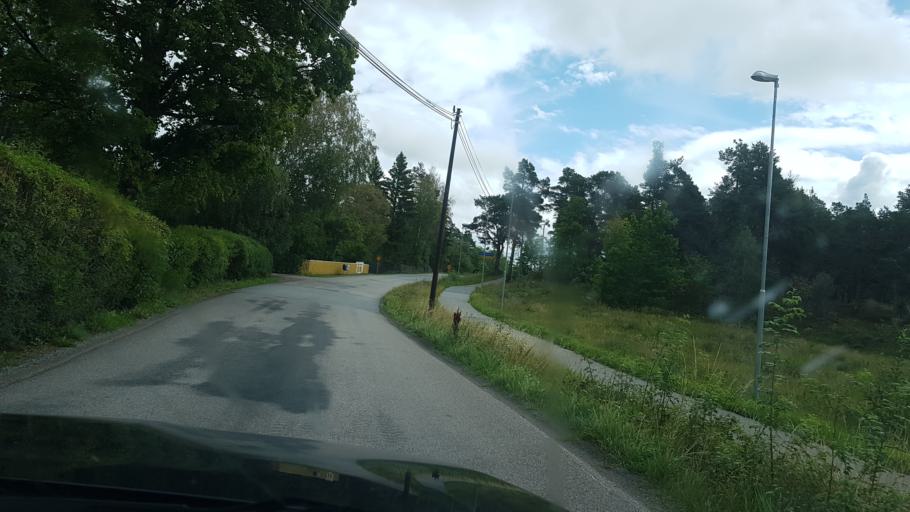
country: SE
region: Uppsala
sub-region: Osthammars Kommun
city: Oregrund
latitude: 60.3506
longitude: 18.4617
